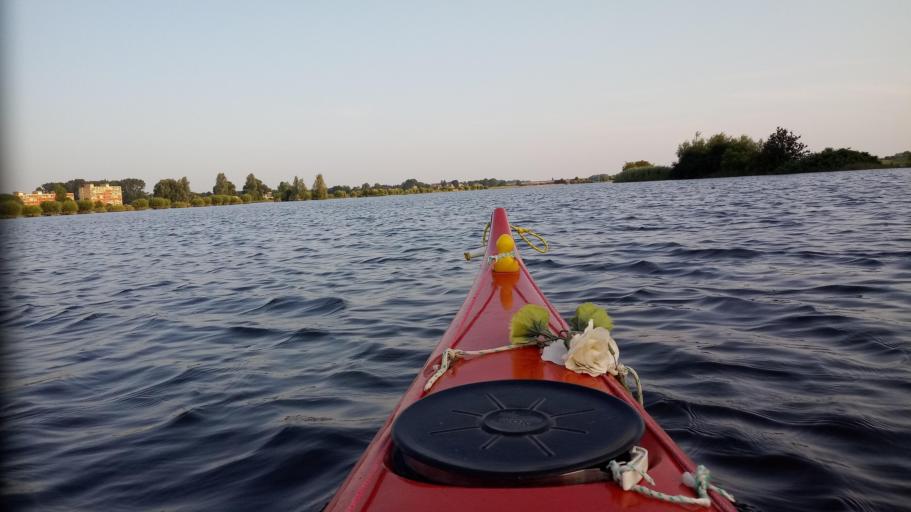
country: NL
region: Gelderland
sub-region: Gemeente Zutphen
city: Zutphen
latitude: 52.1392
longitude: 6.1861
